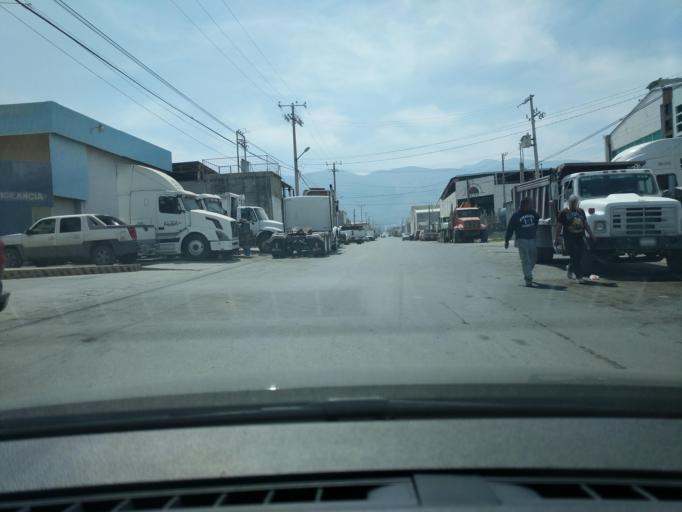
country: MX
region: Coahuila
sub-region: Arteaga
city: Arteaga
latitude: 25.4348
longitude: -100.9111
